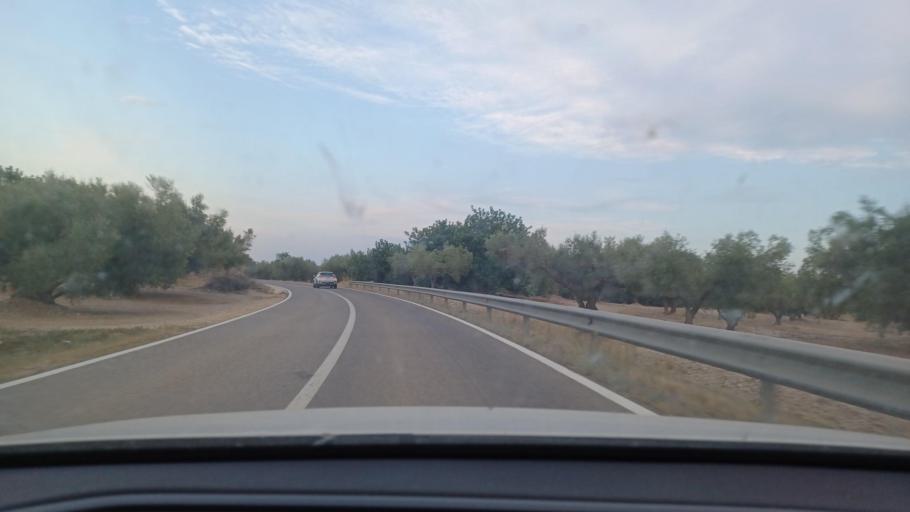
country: ES
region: Catalonia
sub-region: Provincia de Tarragona
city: Mas de Barberans
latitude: 40.7123
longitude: 0.4056
